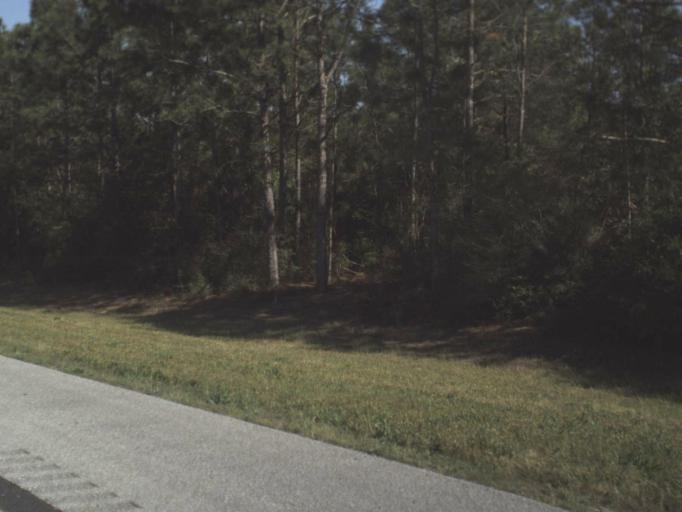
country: US
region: Florida
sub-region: Okaloosa County
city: Crestview
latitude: 30.7151
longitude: -86.6801
